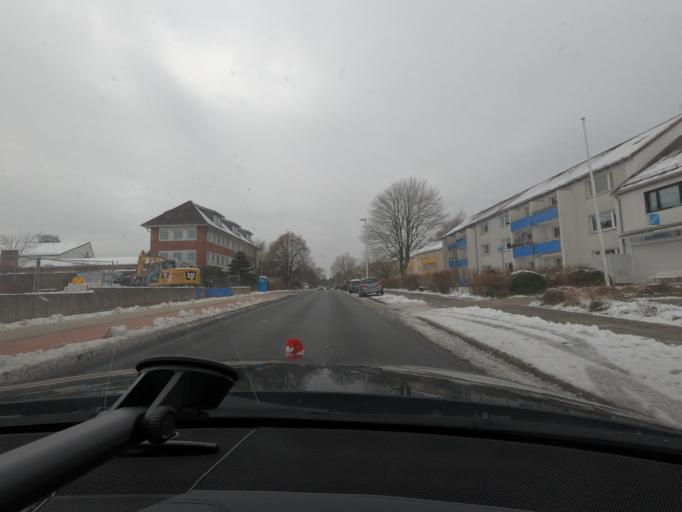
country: DE
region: Schleswig-Holstein
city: Jarplund-Weding
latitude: 54.7603
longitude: 9.3977
